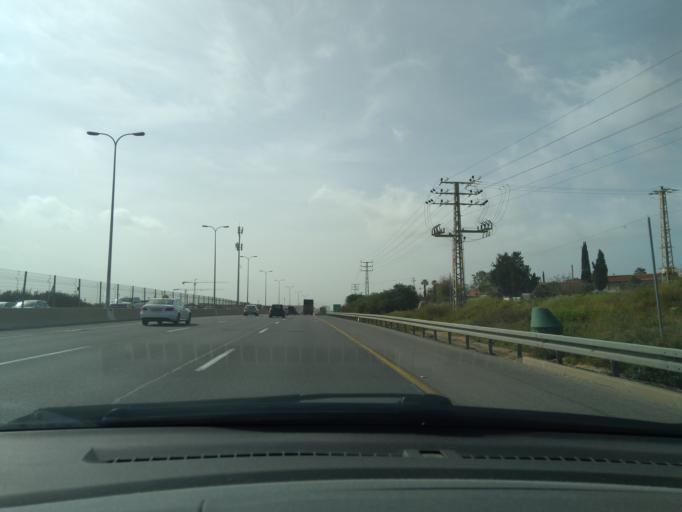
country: IL
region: Central District
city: Netanya
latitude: 32.2972
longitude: 34.8624
